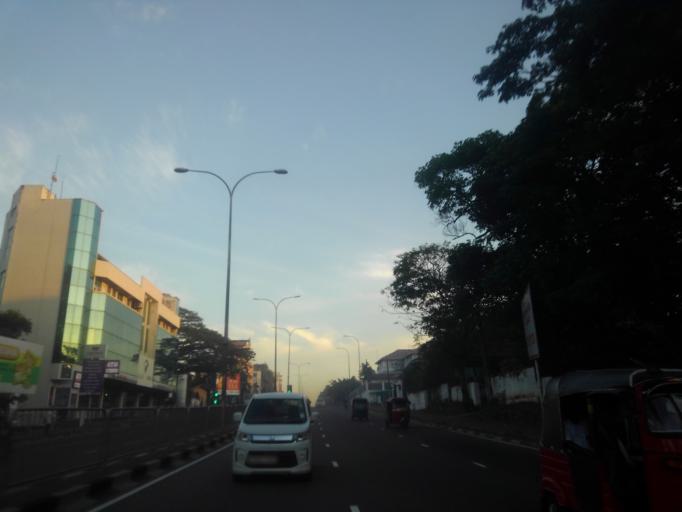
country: LK
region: Western
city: Kolonnawa
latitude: 6.9202
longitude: 79.8778
